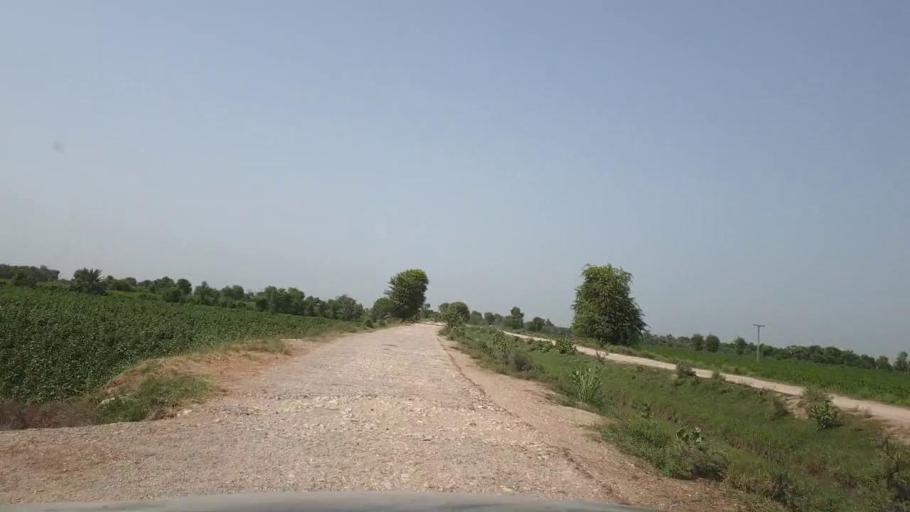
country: PK
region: Sindh
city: Pano Aqil
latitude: 27.8331
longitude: 69.1853
